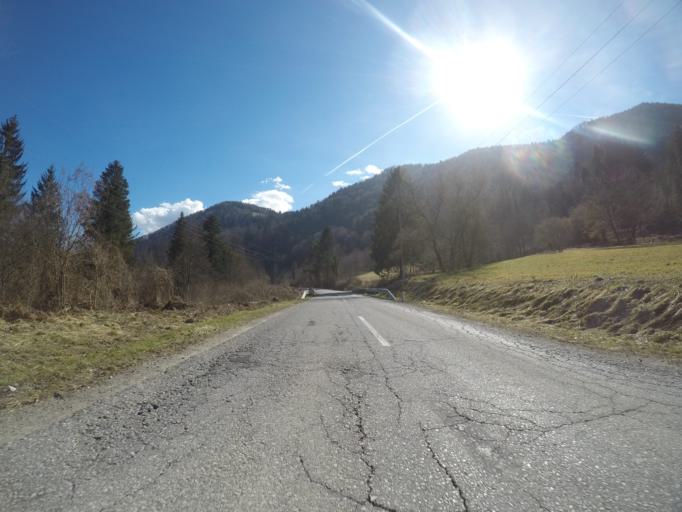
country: SI
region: Selnica ob Dravi
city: Selnica ob Dravi
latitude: 46.5355
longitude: 15.4552
